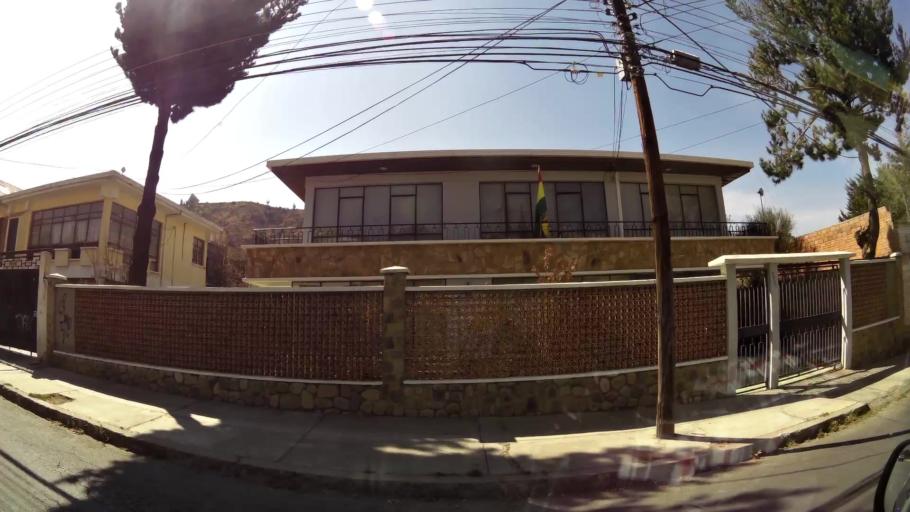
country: BO
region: La Paz
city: La Paz
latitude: -16.5275
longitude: -68.0856
